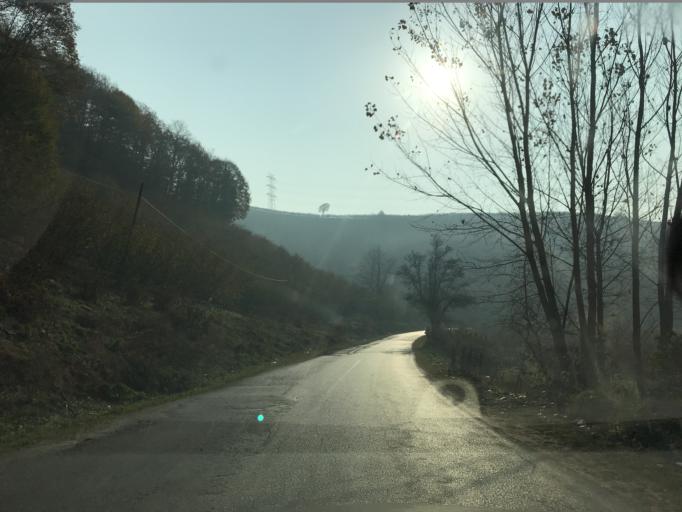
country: TR
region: Duzce
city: Cumayeri
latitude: 40.9032
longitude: 30.9539
